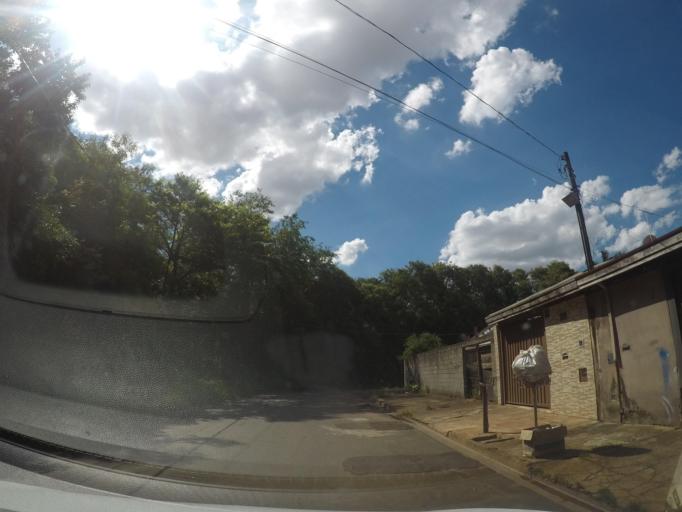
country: BR
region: Sao Paulo
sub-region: Sumare
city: Sumare
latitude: -22.8388
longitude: -47.2705
